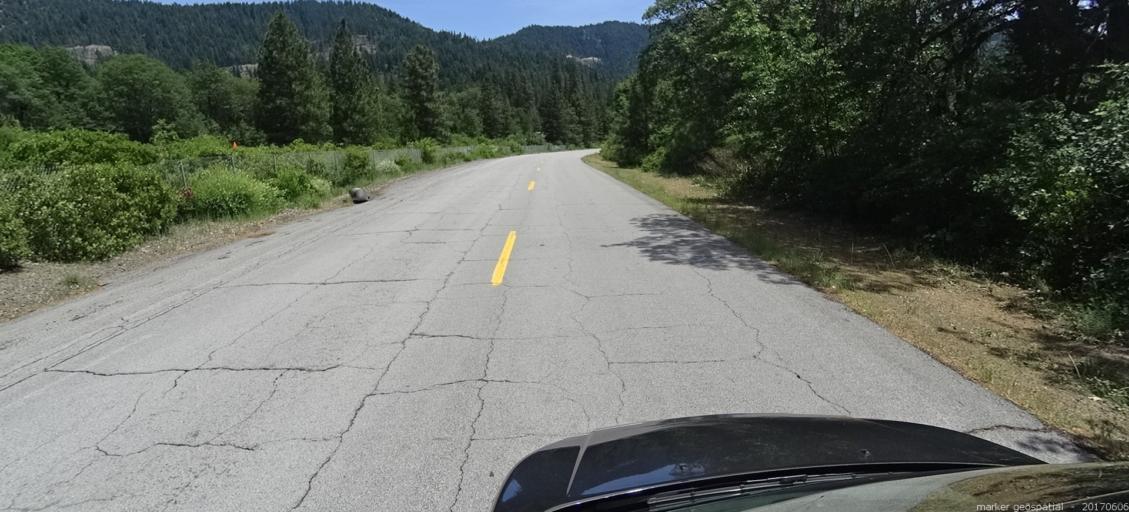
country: US
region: California
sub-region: Siskiyou County
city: Dunsmuir
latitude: 41.2513
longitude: -122.2612
